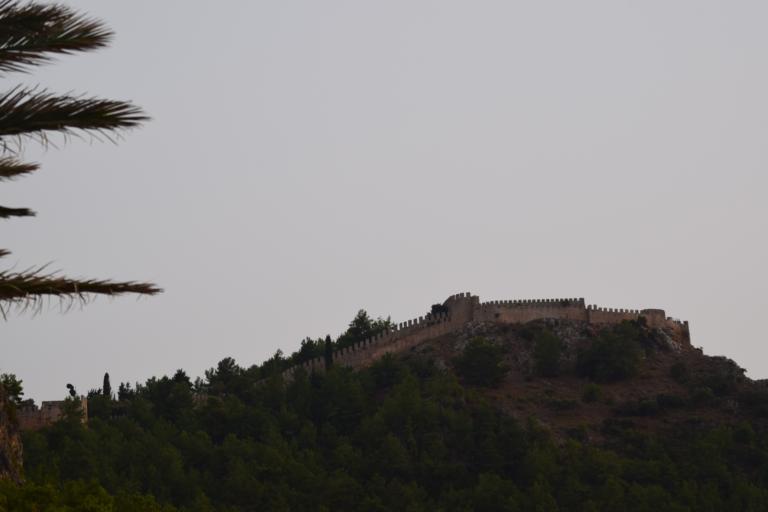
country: TR
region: Antalya
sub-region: Alanya
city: Alanya
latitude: 36.5424
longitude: 31.9887
